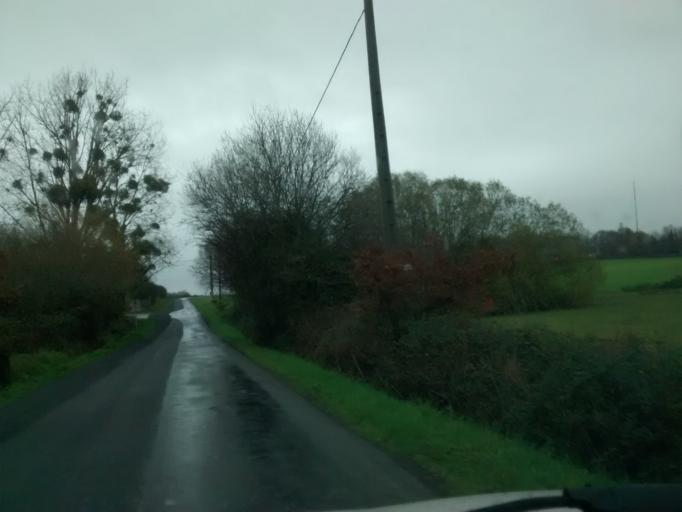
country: FR
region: Brittany
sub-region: Departement d'Ille-et-Vilaine
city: Cesson-Sevigne
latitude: 48.1005
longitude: -1.5906
